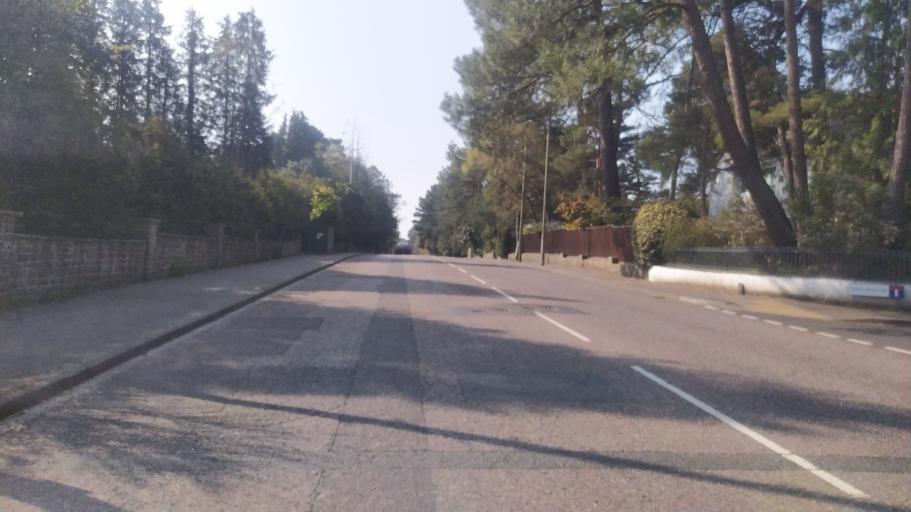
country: GB
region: England
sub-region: Dorset
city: Parkstone
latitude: 50.7128
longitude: -1.9260
